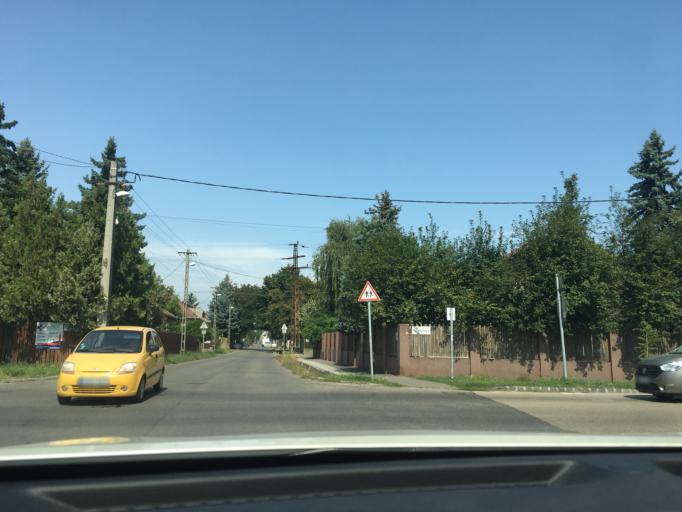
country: HU
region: Budapest
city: Budapest XVII. keruelet
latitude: 47.4872
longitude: 19.2709
